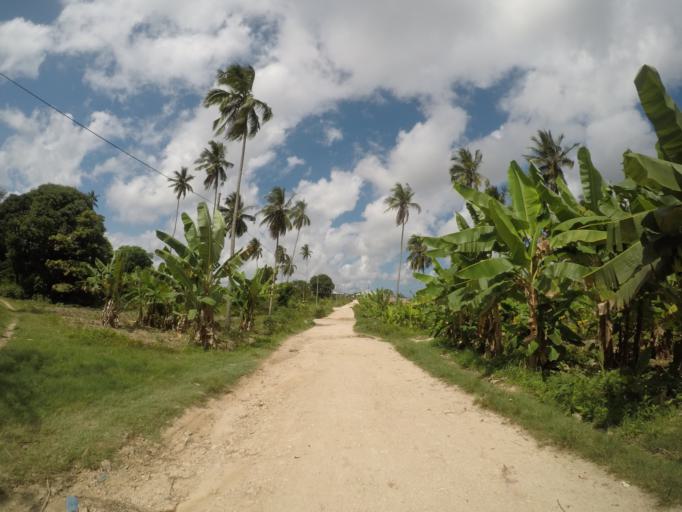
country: TZ
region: Pemba South
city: Chake Chake
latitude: -5.2335
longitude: 39.7798
